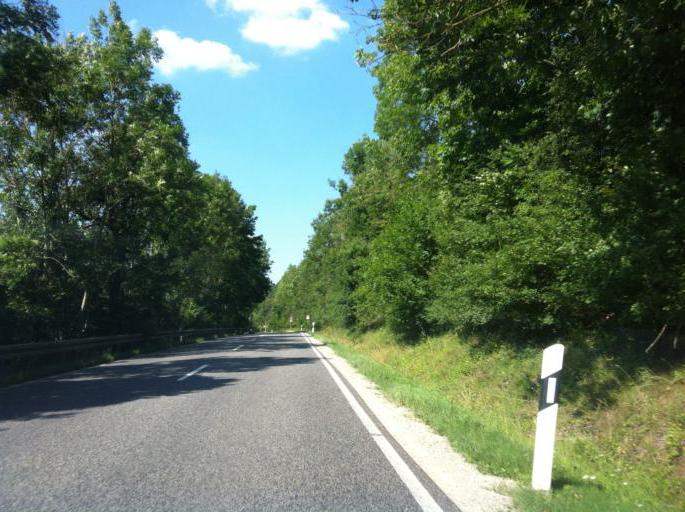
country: DE
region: Thuringia
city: Geisleden
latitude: 51.3541
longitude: 10.1867
